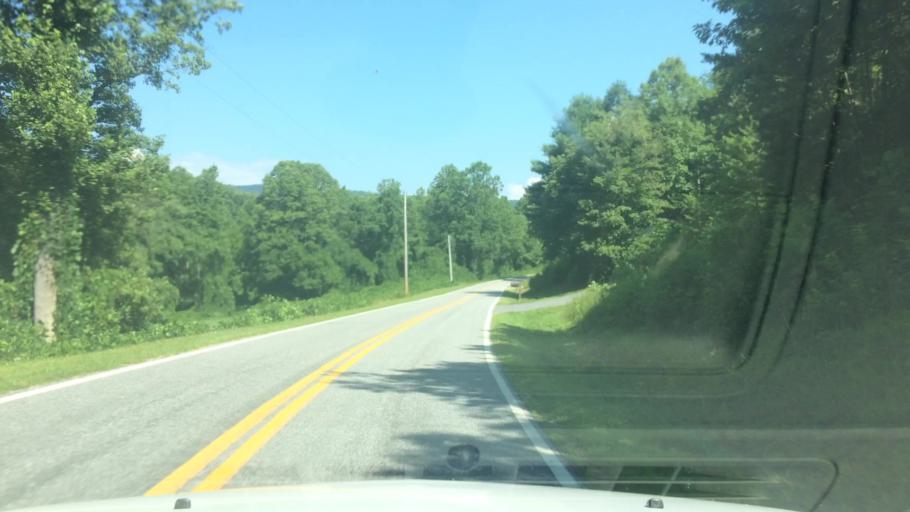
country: US
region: North Carolina
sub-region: Alexander County
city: Taylorsville
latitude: 35.9767
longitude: -81.2758
